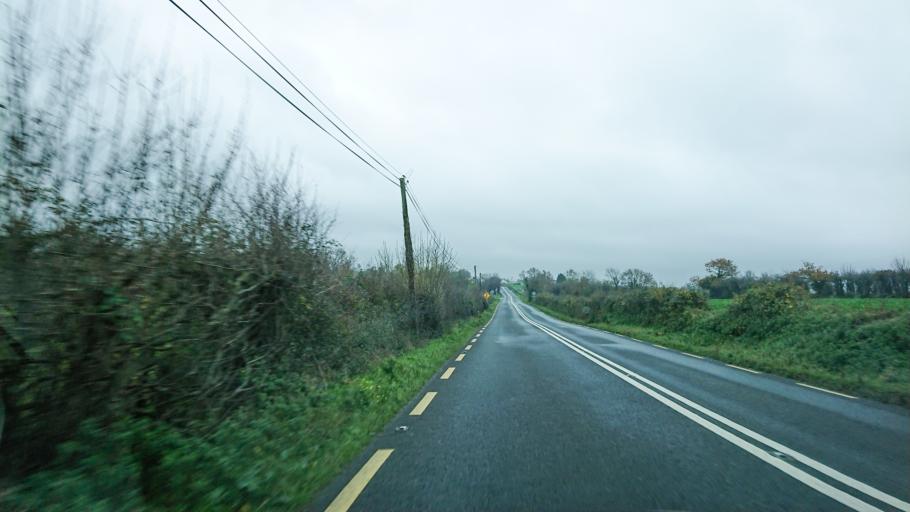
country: IE
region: Leinster
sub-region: Kilkenny
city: Mooncoin
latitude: 52.3071
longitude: -7.2812
